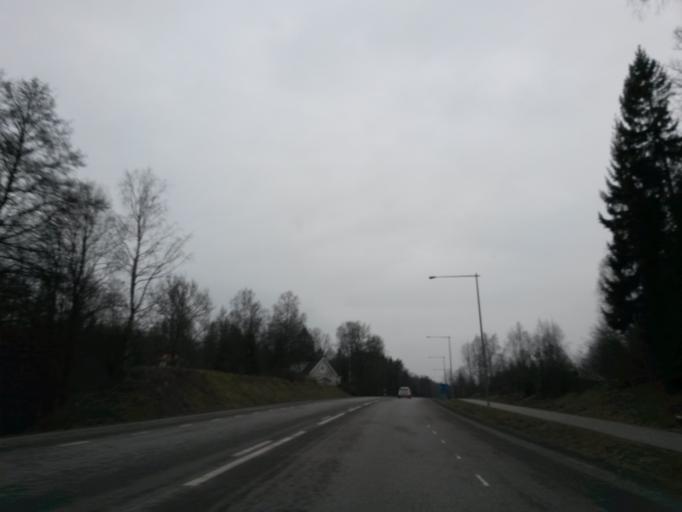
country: SE
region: Vaestra Goetaland
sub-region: Boras Kommun
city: Ganghester
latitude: 57.7949
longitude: 13.0087
